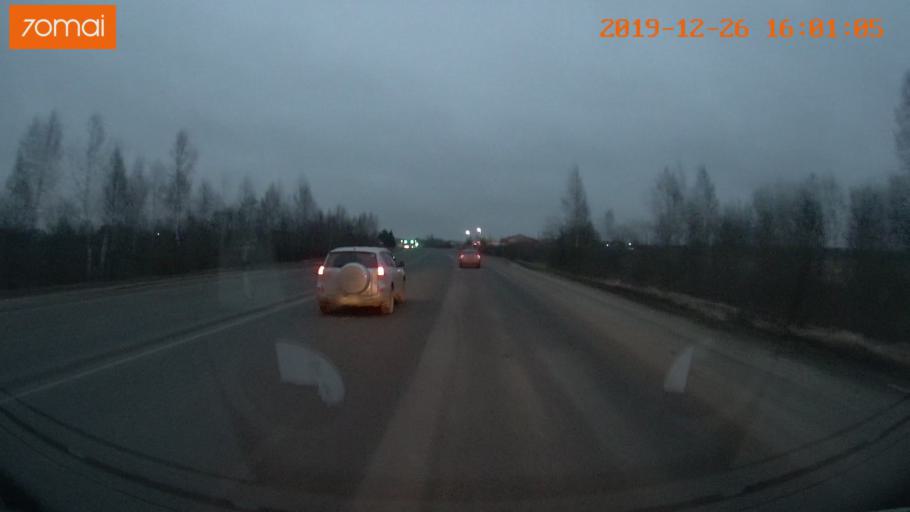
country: RU
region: Jaroslavl
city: Rybinsk
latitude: 58.0179
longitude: 38.8133
